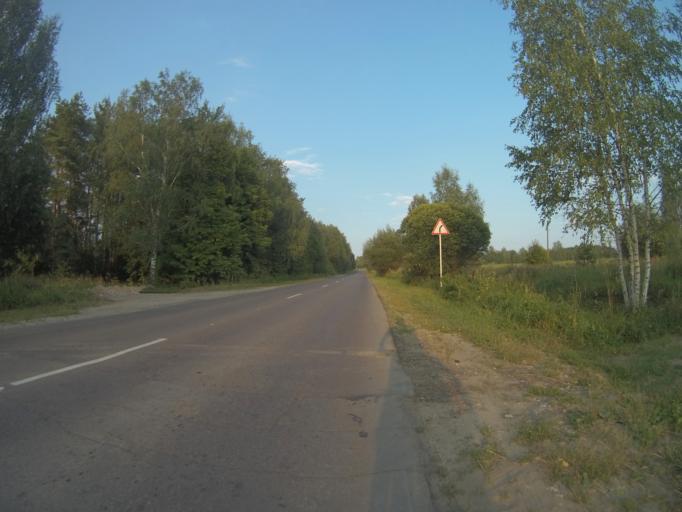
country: RU
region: Vladimir
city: Orgtrud
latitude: 56.2516
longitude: 40.5769
